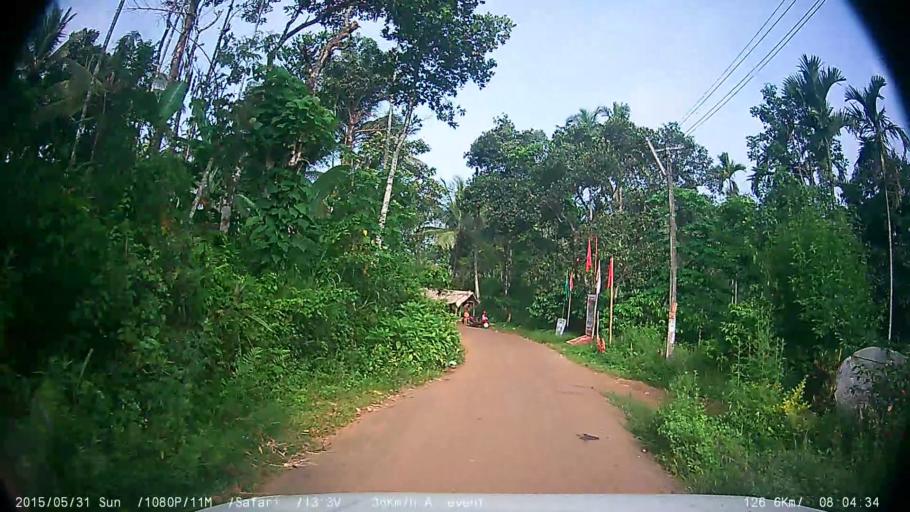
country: IN
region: Kerala
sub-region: Wayanad
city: Kalpetta
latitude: 11.6358
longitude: 76.0387
